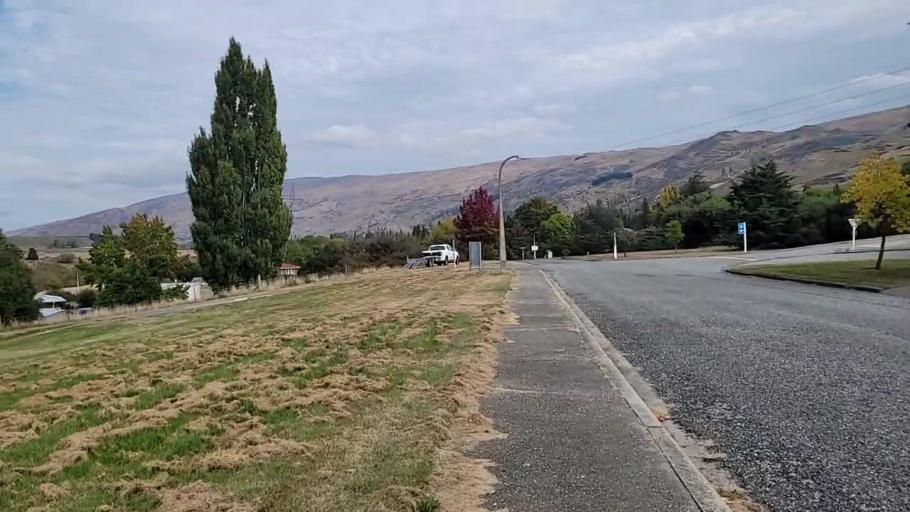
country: NZ
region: Otago
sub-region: Queenstown-Lakes District
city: Kingston
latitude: -45.4773
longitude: 169.3175
